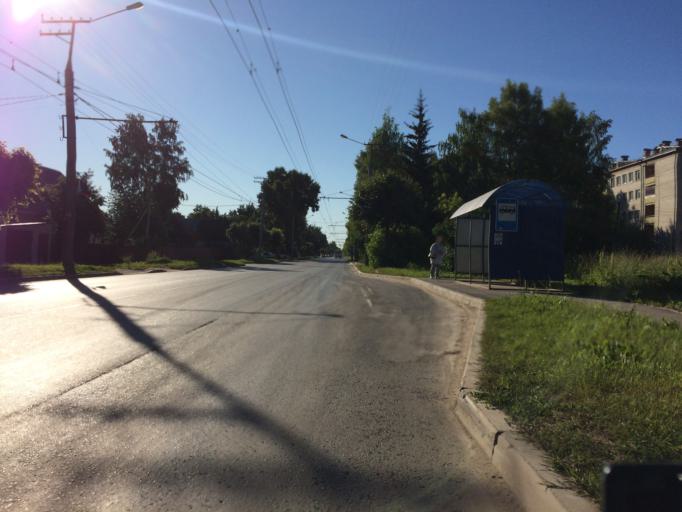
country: RU
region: Mariy-El
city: Yoshkar-Ola
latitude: 56.6532
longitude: 47.8790
